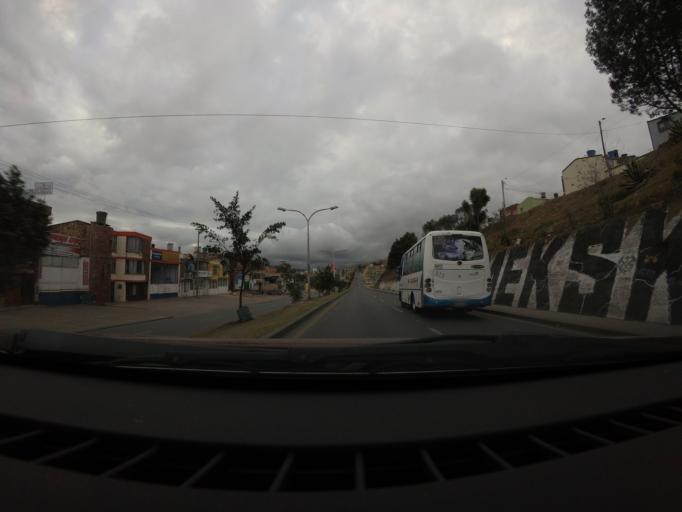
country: CO
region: Boyaca
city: Tunja
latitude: 5.5208
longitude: -73.3646
